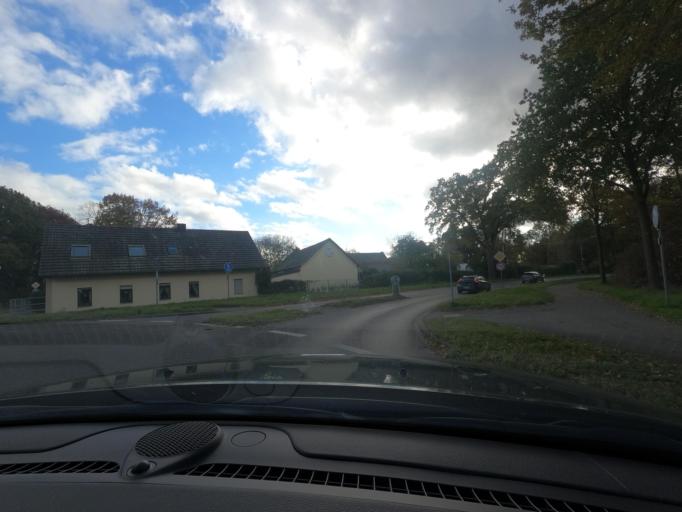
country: DE
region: North Rhine-Westphalia
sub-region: Regierungsbezirk Dusseldorf
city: Bruggen
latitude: 51.2523
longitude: 6.2152
